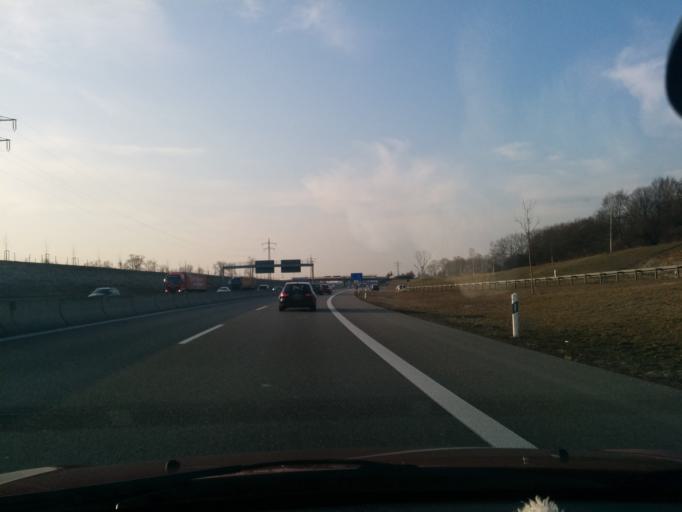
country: DE
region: Bavaria
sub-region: Upper Bavaria
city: Germering
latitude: 48.1296
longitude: 11.4021
